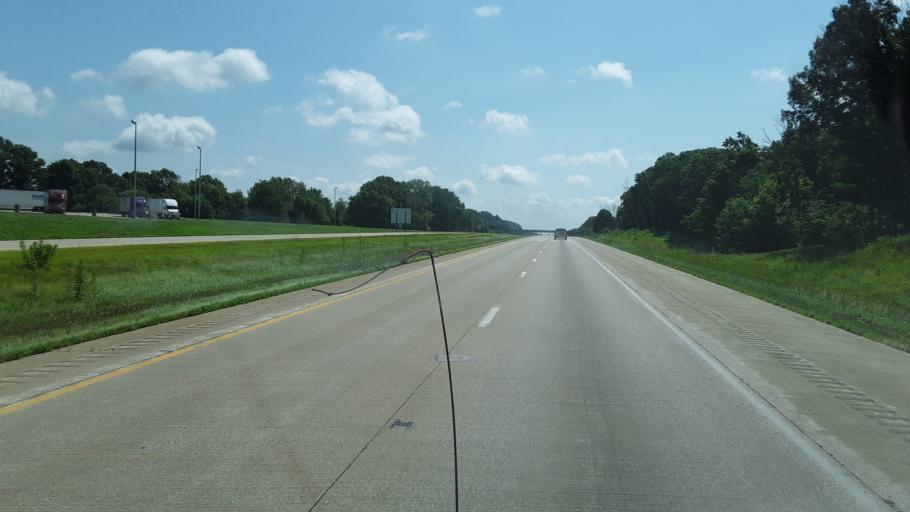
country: US
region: Illinois
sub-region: Clark County
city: Marshall
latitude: 39.4217
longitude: -87.6614
